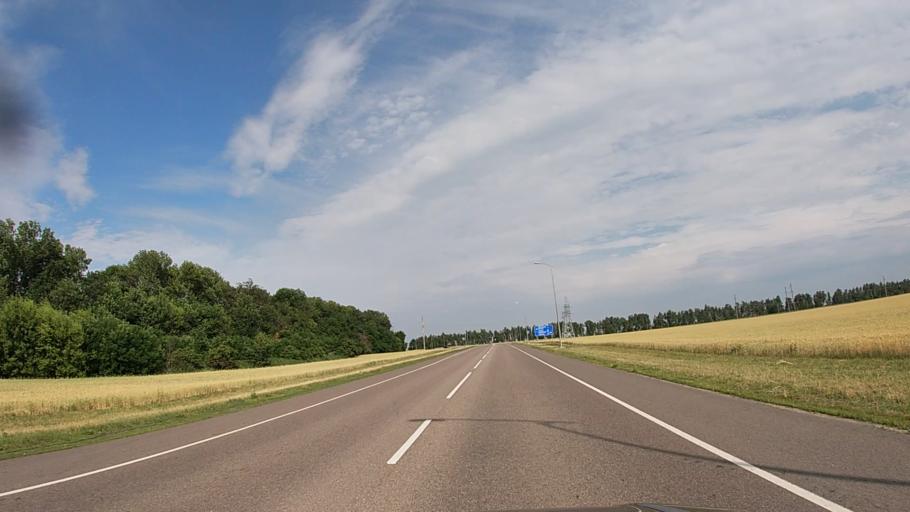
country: RU
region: Belgorod
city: Proletarskiy
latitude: 50.8296
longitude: 35.7710
